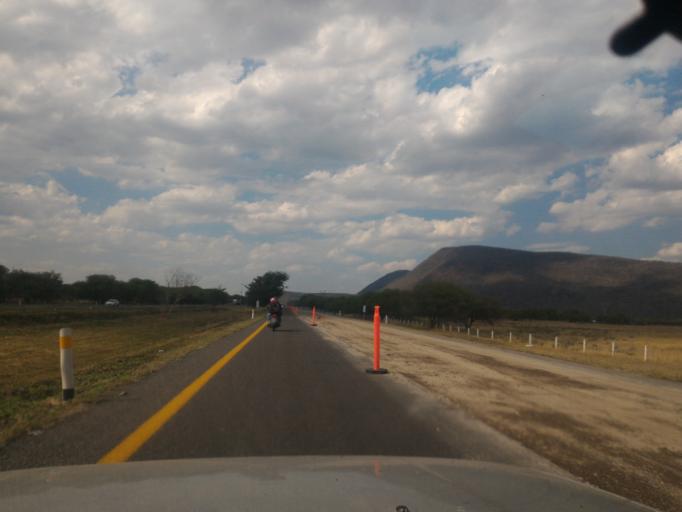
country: MX
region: Jalisco
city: Zacoalco de Torres
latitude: 20.1656
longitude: -103.5033
